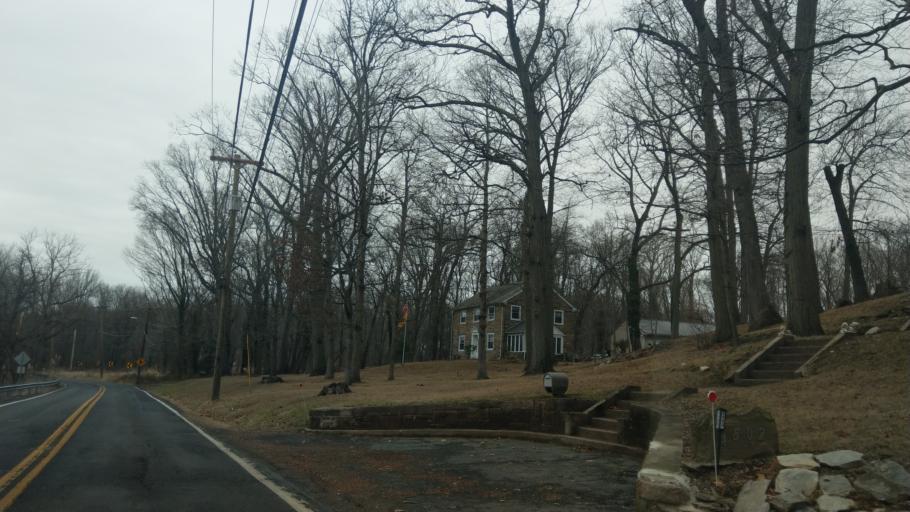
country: US
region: Pennsylvania
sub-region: Bucks County
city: Hulmeville
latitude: 40.1308
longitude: -74.8981
